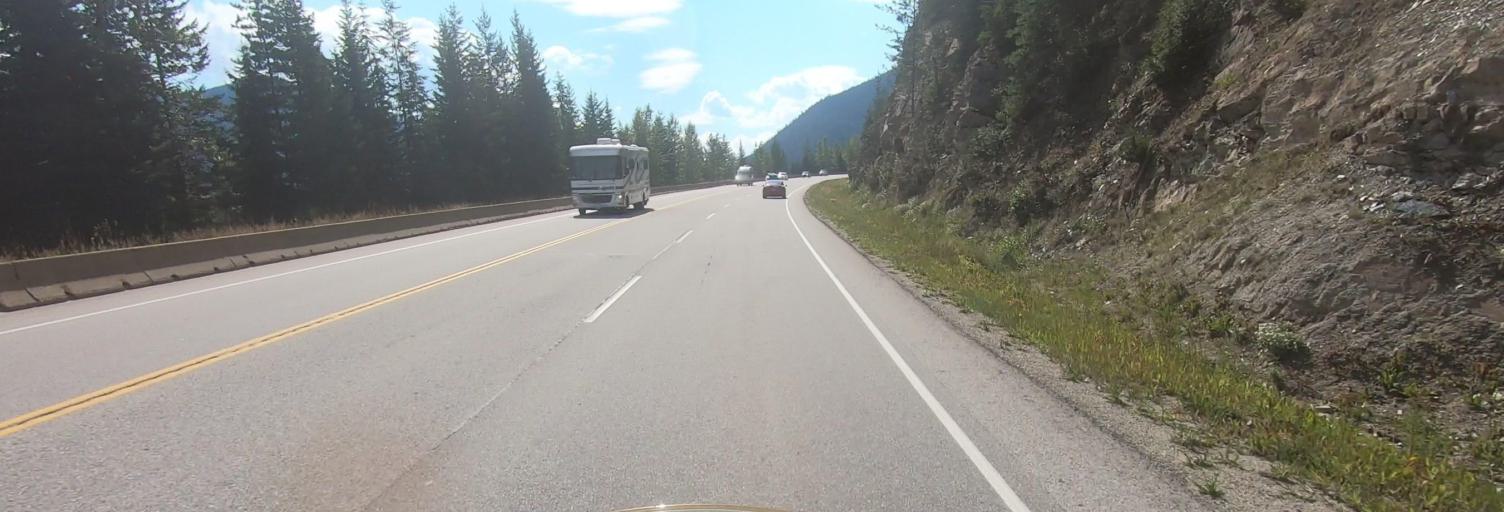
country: CA
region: British Columbia
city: Golden
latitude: 51.3621
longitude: -117.4394
